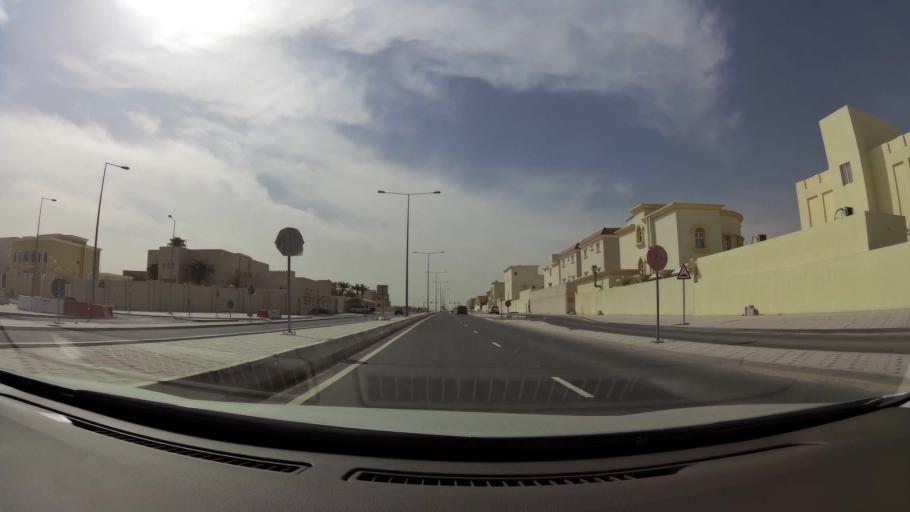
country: QA
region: Baladiyat ar Rayyan
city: Ar Rayyan
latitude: 25.3235
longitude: 51.3921
